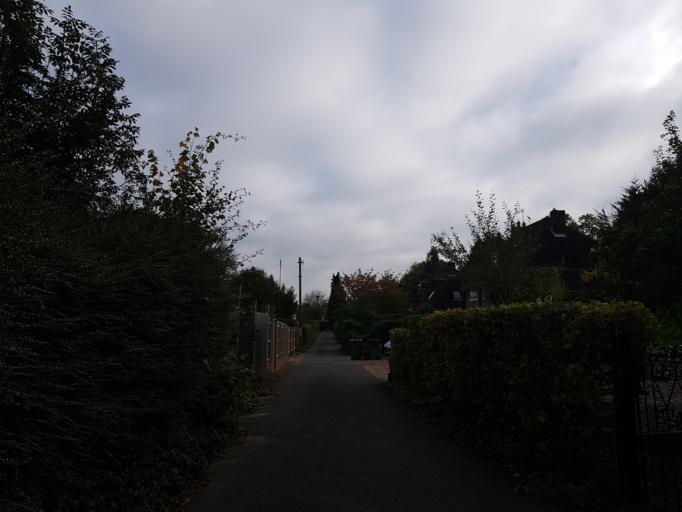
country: GB
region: England
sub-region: Surrey
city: Guildford
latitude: 51.2326
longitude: -0.5963
